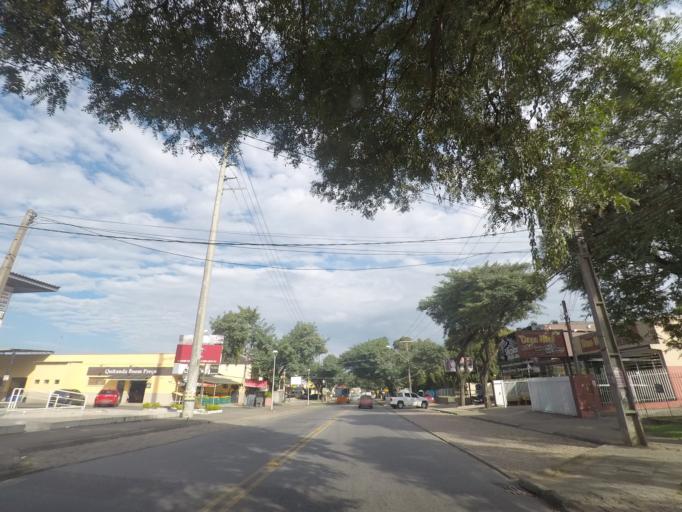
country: BR
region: Parana
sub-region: Sao Jose Dos Pinhais
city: Sao Jose dos Pinhais
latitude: -25.5368
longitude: -49.2951
